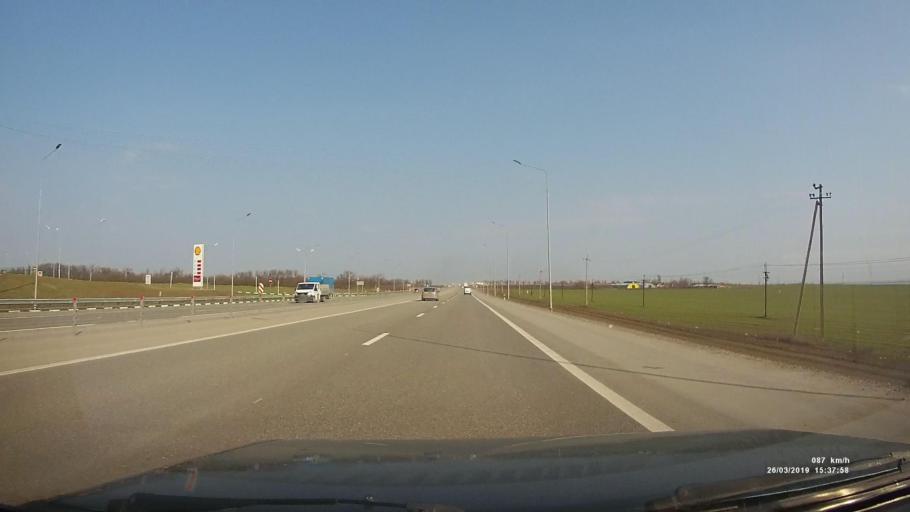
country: RU
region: Rostov
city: Sinyavskoye
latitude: 47.2959
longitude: 39.2581
